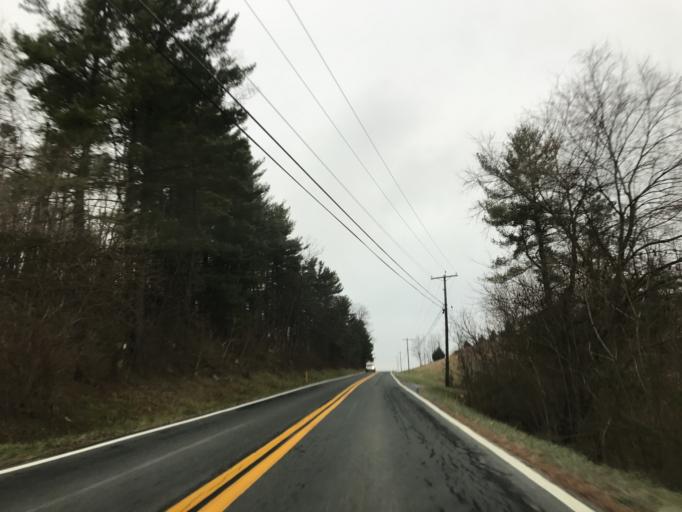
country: US
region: Maryland
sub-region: Carroll County
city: Westminster
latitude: 39.5392
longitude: -77.0436
